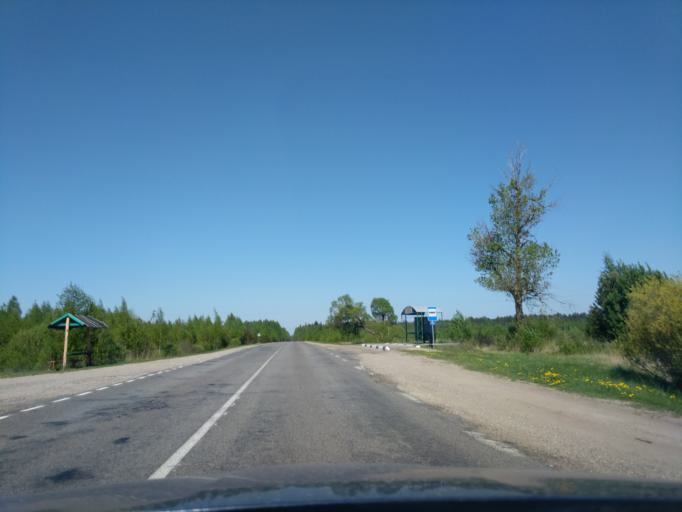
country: BY
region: Minsk
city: Il'ya
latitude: 54.3979
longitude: 27.3342
